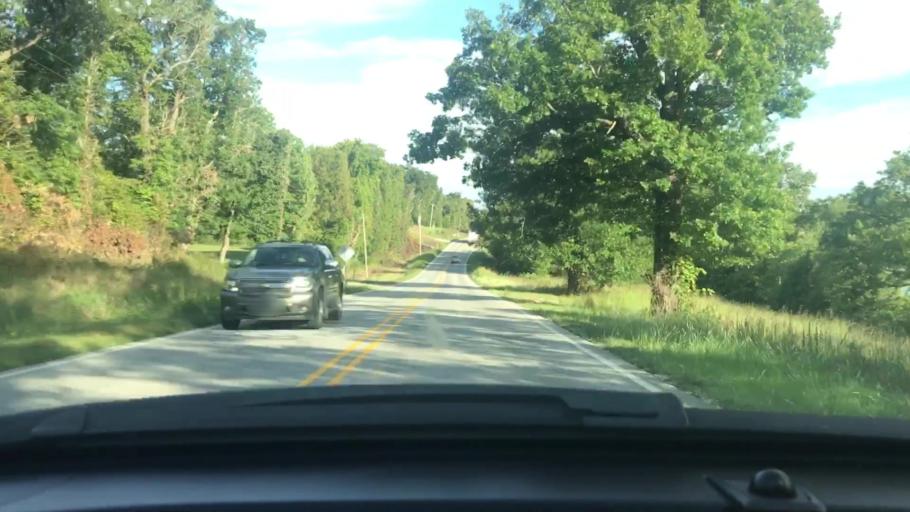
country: US
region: Arkansas
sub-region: Sharp County
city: Cherokee Village
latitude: 36.3083
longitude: -91.4571
